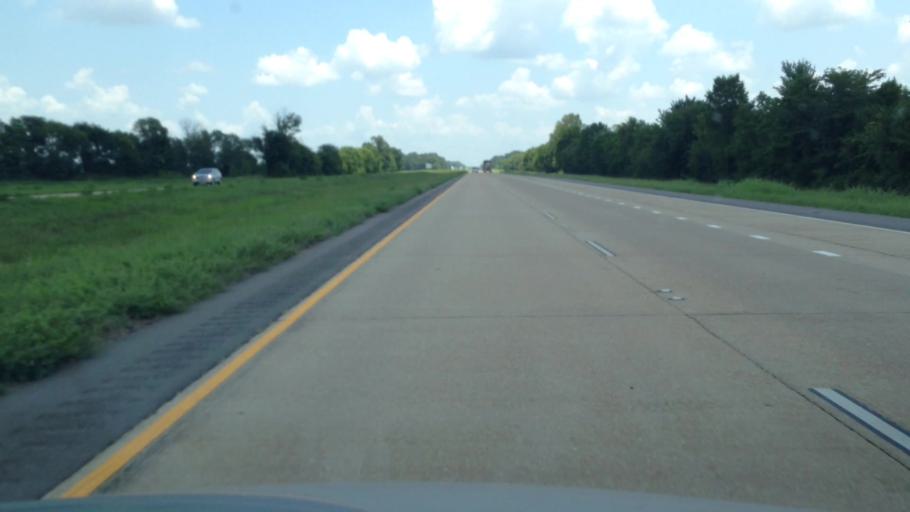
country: US
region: Louisiana
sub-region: Rapides Parish
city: Lecompte
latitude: 31.0122
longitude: -92.3703
